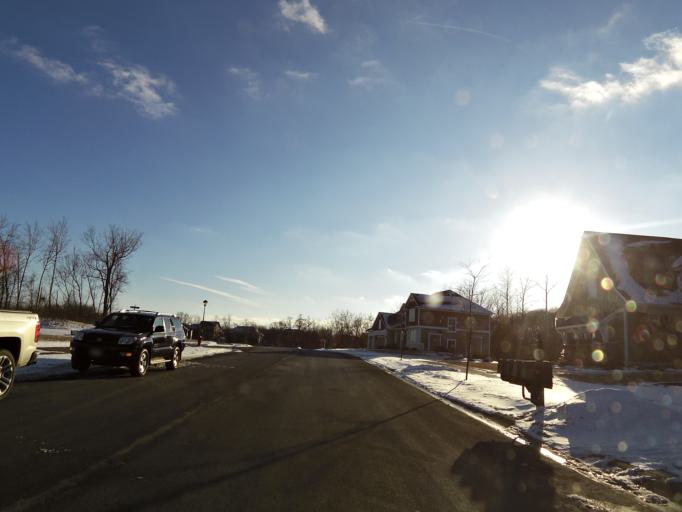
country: US
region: Minnesota
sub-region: Scott County
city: Prior Lake
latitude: 44.7444
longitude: -93.4510
